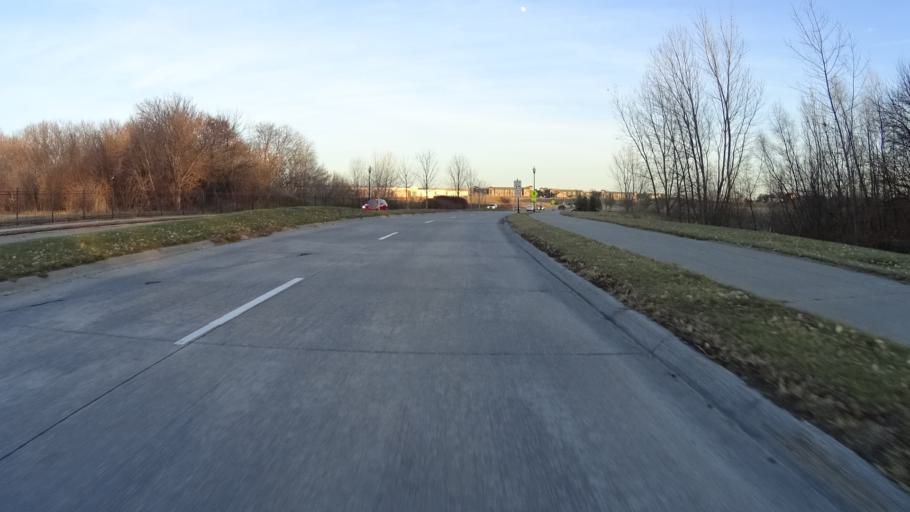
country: US
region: Nebraska
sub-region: Sarpy County
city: Papillion
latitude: 41.1330
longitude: -96.0358
